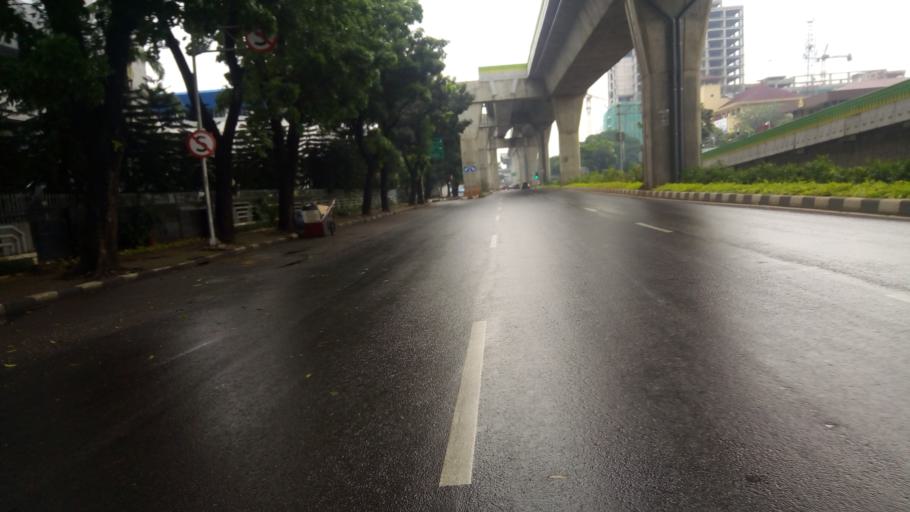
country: ID
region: Jakarta Raya
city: Jakarta
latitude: -6.2400
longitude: 106.8039
